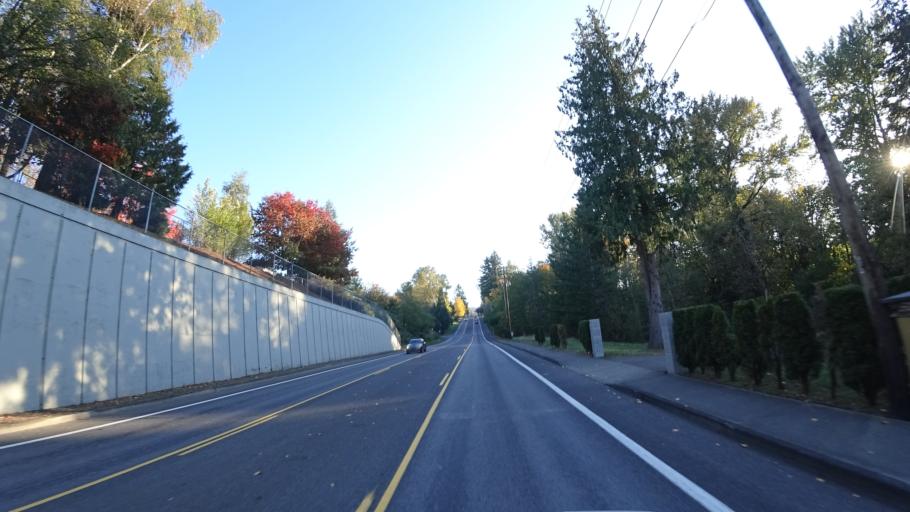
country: US
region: Oregon
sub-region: Multnomah County
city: Gresham
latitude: 45.4884
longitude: -122.4480
